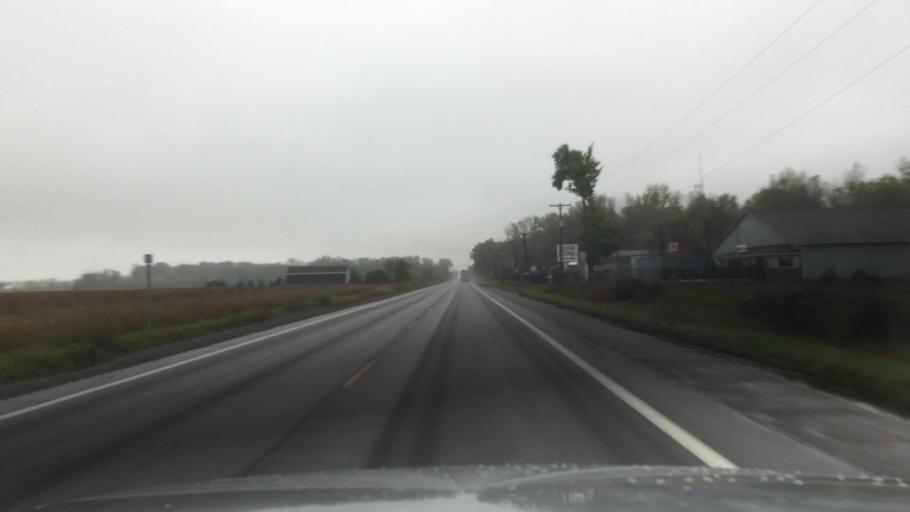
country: US
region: Michigan
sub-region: Saginaw County
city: Saginaw
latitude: 43.3768
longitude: -83.9552
